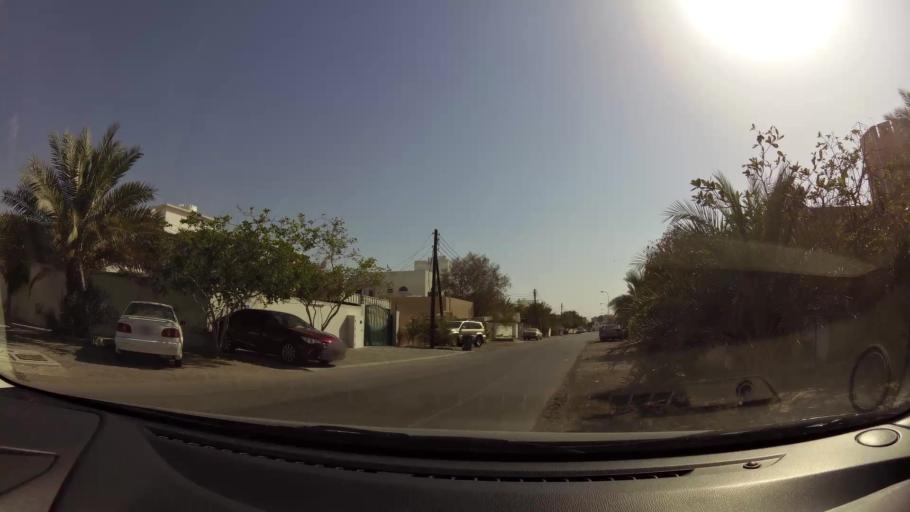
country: OM
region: Muhafazat Masqat
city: As Sib al Jadidah
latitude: 23.6293
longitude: 58.2075
